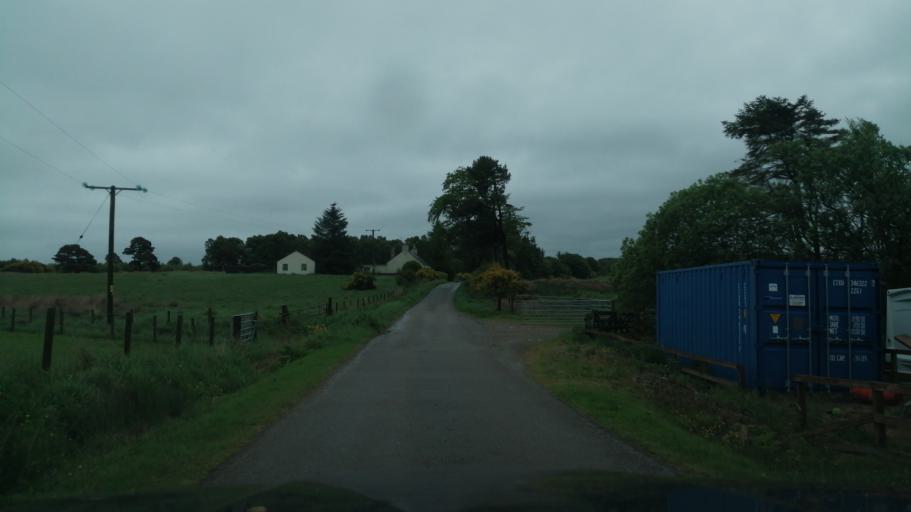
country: GB
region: Scotland
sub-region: Moray
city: Keith
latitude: 57.5688
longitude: -2.8609
